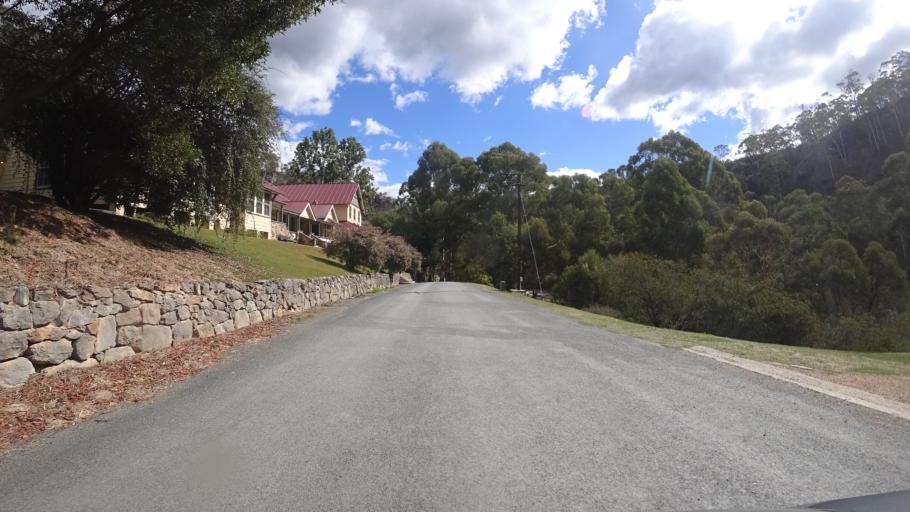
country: AU
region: New South Wales
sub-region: Tumut Shire
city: Tumut
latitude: -35.7253
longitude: 148.4913
